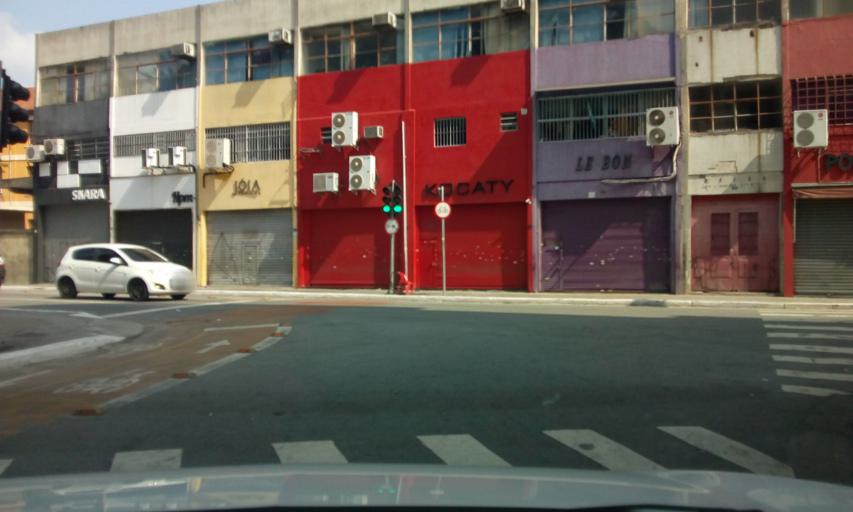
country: BR
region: Sao Paulo
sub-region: Sao Paulo
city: Sao Paulo
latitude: -23.5335
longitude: -46.6373
